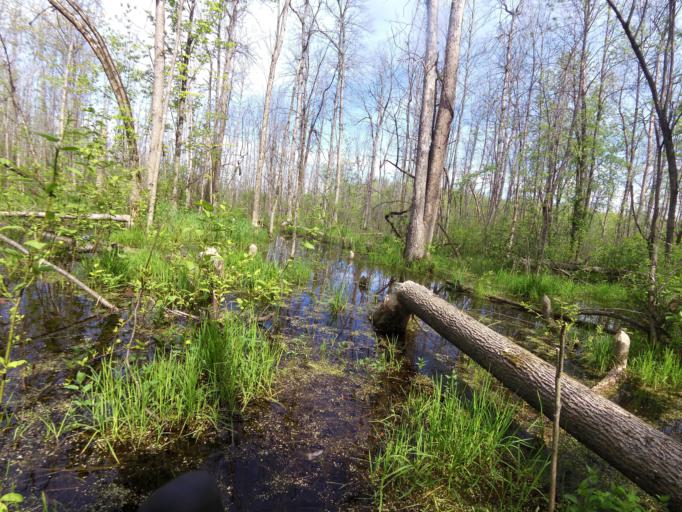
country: CA
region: Ontario
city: Ottawa
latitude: 45.3356
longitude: -75.6217
